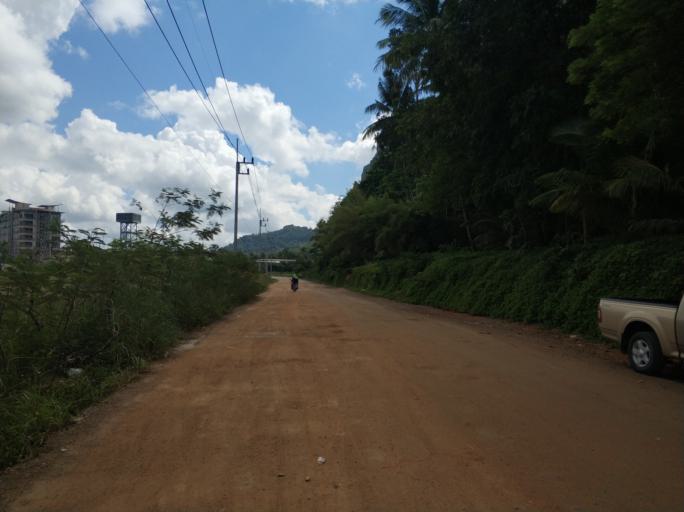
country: TH
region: Phangnga
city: Ban Ao Nang
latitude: 8.0303
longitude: 98.8272
